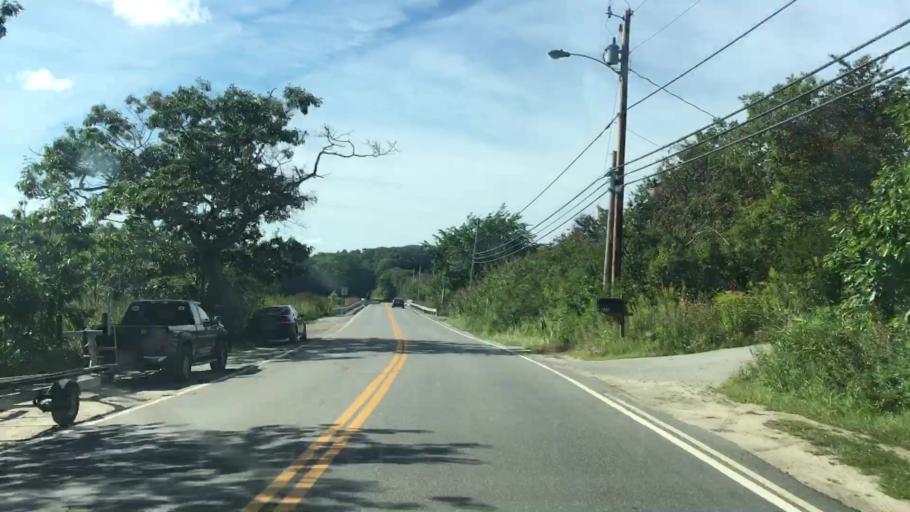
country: US
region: Maine
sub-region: Sagadahoc County
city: Bath
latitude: 43.9309
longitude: -69.8607
